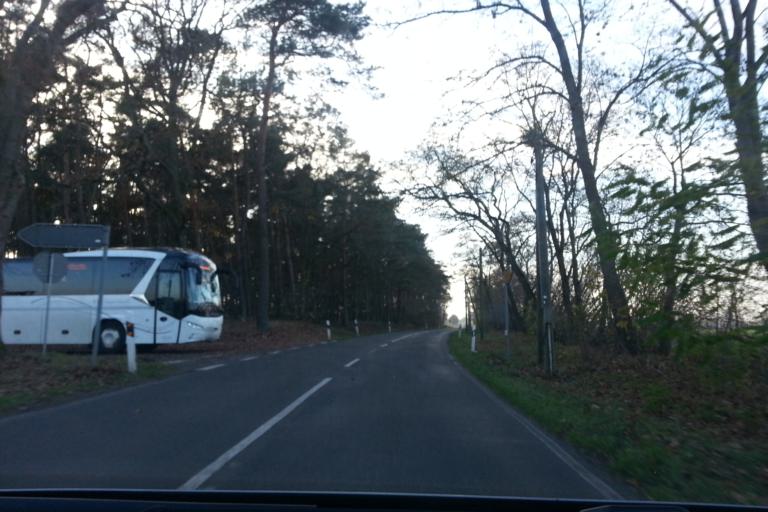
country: DE
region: Mecklenburg-Vorpommern
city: Ferdinandshof
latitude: 53.6350
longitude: 13.8420
